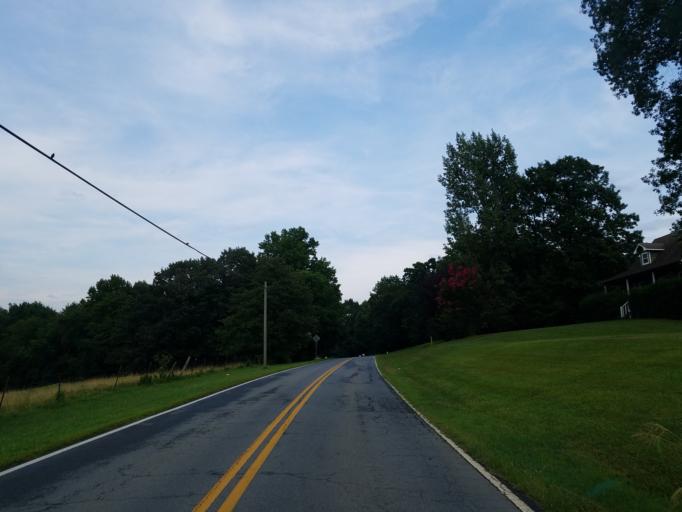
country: US
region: Georgia
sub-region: Pickens County
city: Jasper
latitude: 34.4666
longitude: -84.5129
